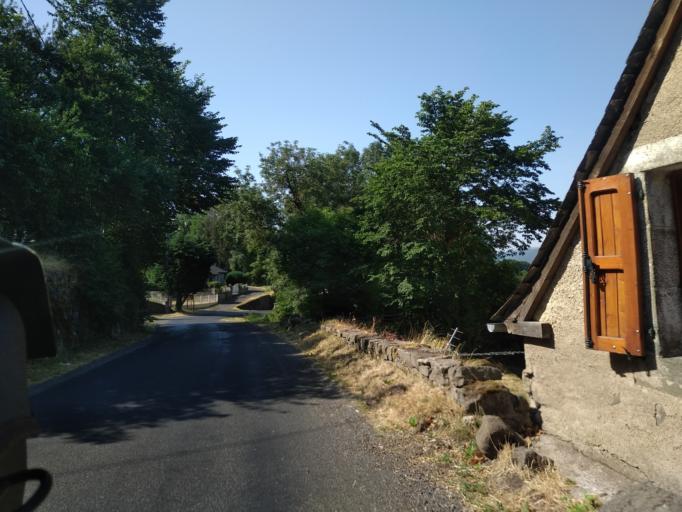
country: FR
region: Auvergne
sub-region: Departement du Cantal
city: Riom-es-Montagnes
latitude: 45.2445
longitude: 2.7415
